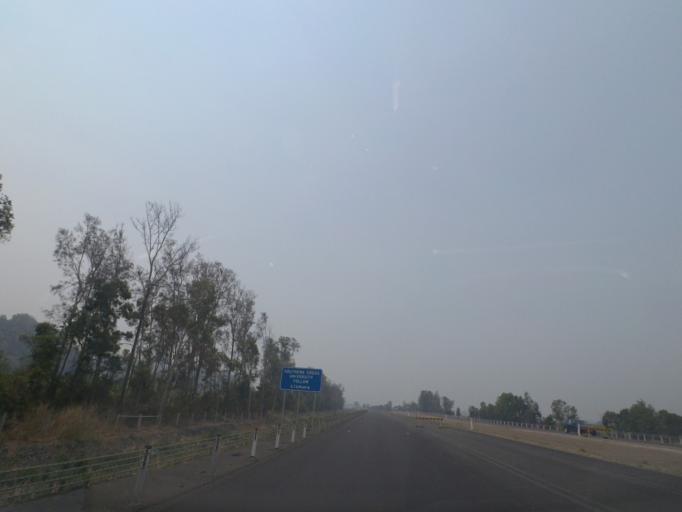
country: AU
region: New South Wales
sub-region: Ballina
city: Ballina
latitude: -28.8800
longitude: 153.4864
